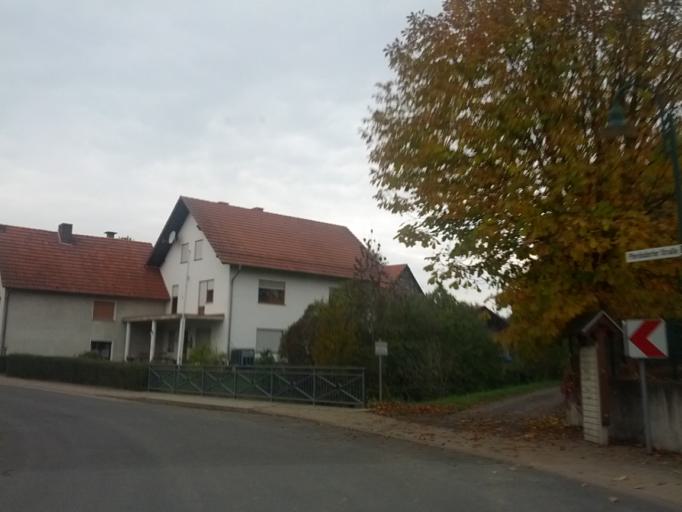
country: DE
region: Hesse
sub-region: Regierungsbezirk Kassel
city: Herleshausen
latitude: 51.0362
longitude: 10.1851
